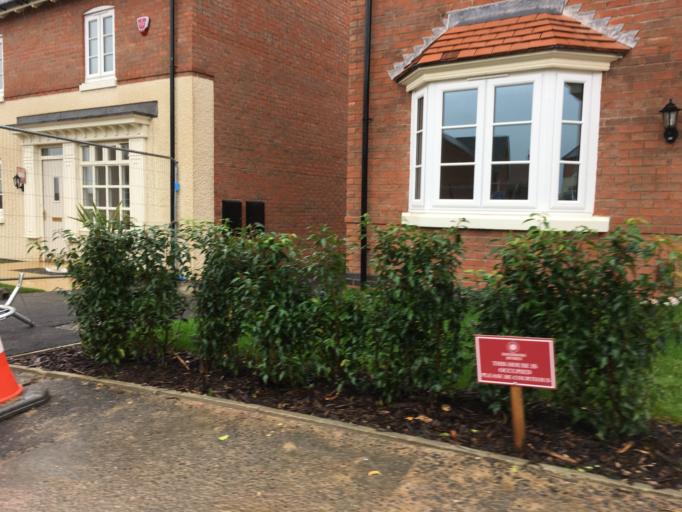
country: GB
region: England
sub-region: Warwickshire
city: Rugby
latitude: 52.3584
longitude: -1.1822
